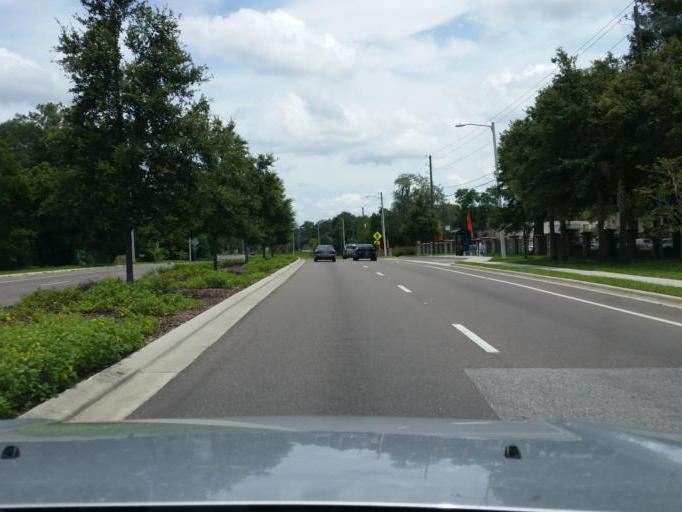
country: US
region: Florida
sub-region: Hillsborough County
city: Temple Terrace
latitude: 28.0169
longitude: -82.4142
